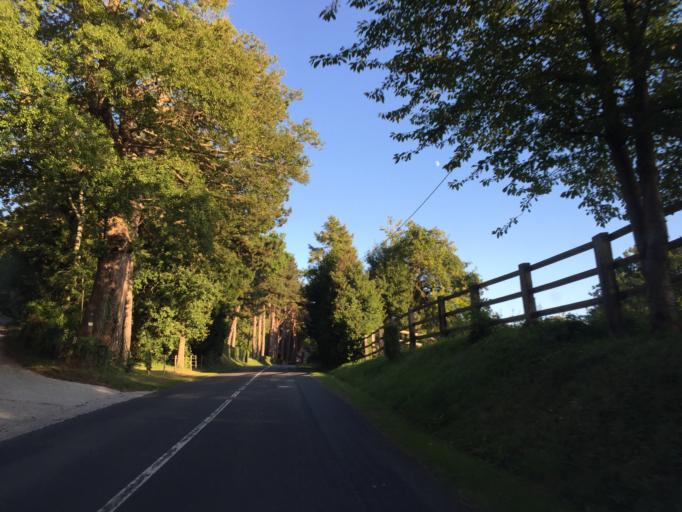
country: FR
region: Lower Normandy
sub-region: Departement du Calvados
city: Equemauville
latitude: 49.4059
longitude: 0.1778
